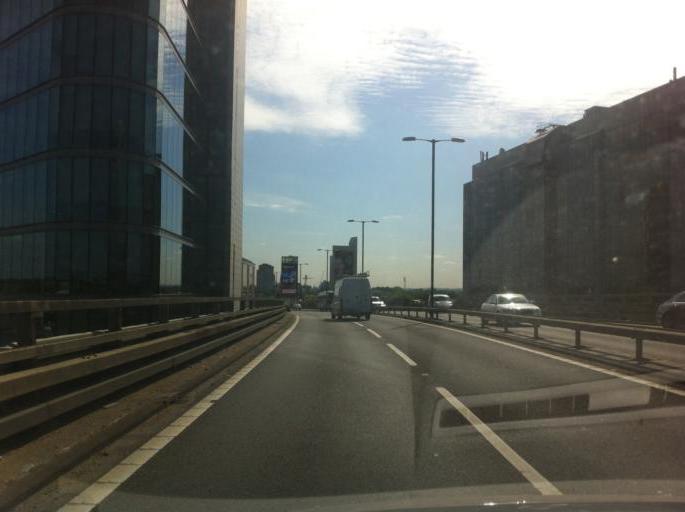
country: GB
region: England
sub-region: Greater London
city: Brentford
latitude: 51.4893
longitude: -0.3149
